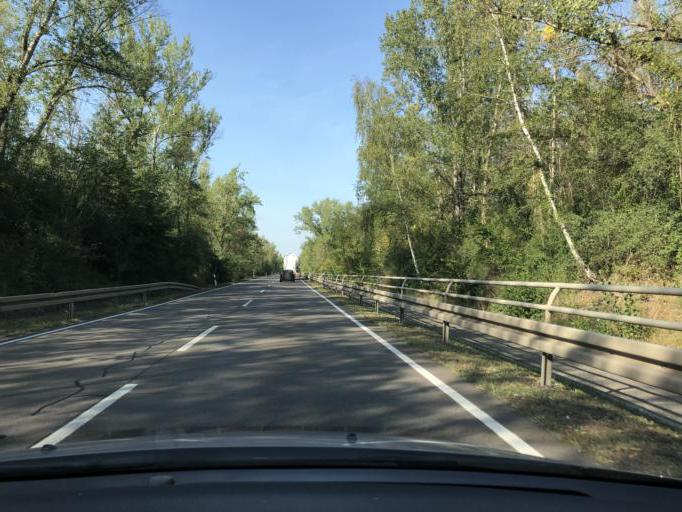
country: DE
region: Saxony-Anhalt
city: Grosskayna
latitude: 51.2955
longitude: 11.9164
